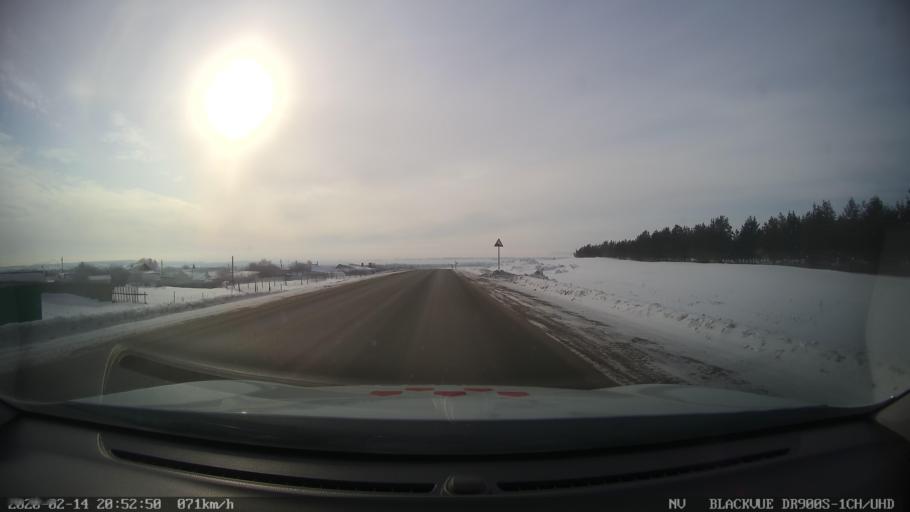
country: RU
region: Tatarstan
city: Kuybyshevskiy Zaton
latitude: 55.2003
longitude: 49.2494
